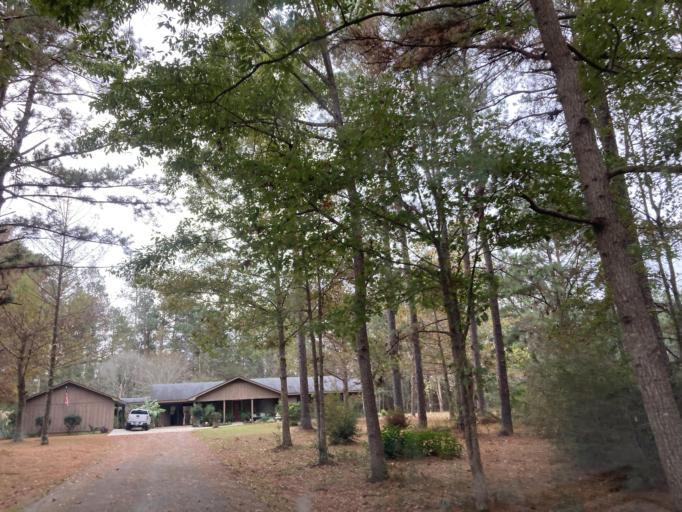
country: US
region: Mississippi
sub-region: Lamar County
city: Purvis
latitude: 31.1577
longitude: -89.4592
